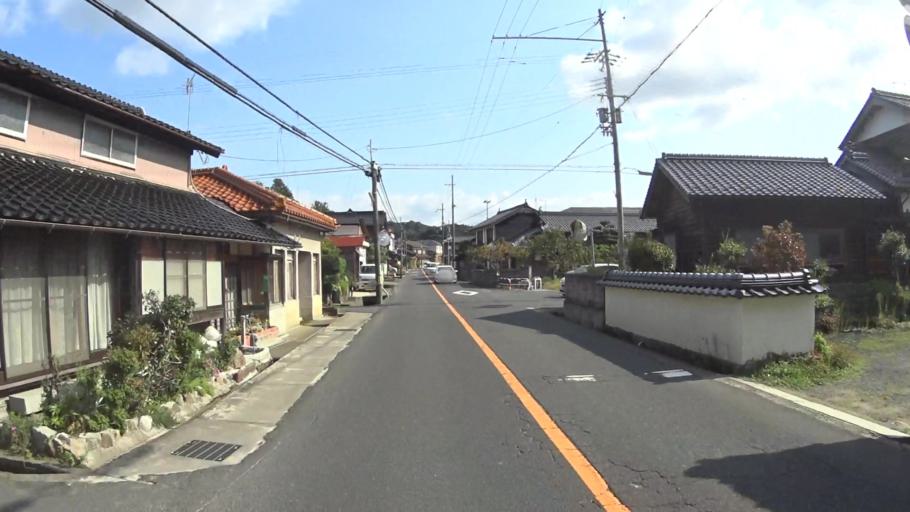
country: JP
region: Kyoto
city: Miyazu
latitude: 35.5895
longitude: 135.1011
